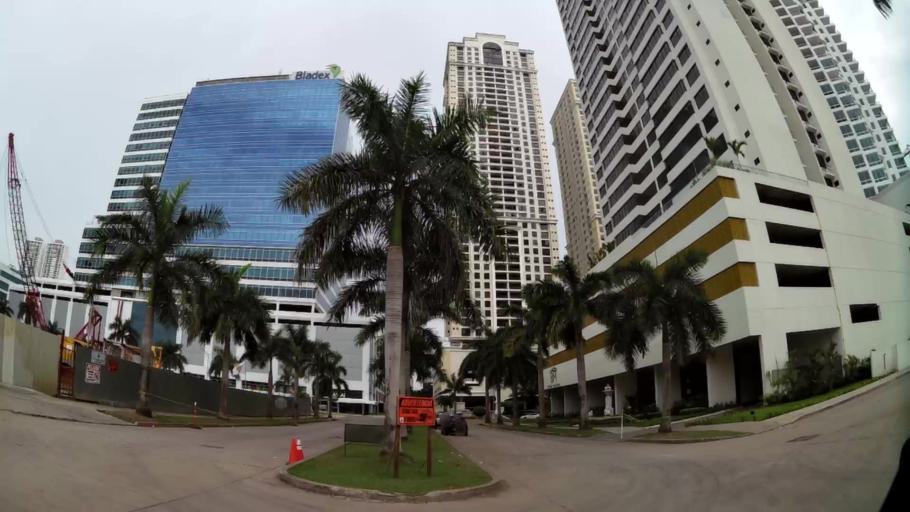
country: PA
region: Panama
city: San Miguelito
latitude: 9.0099
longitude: -79.4724
